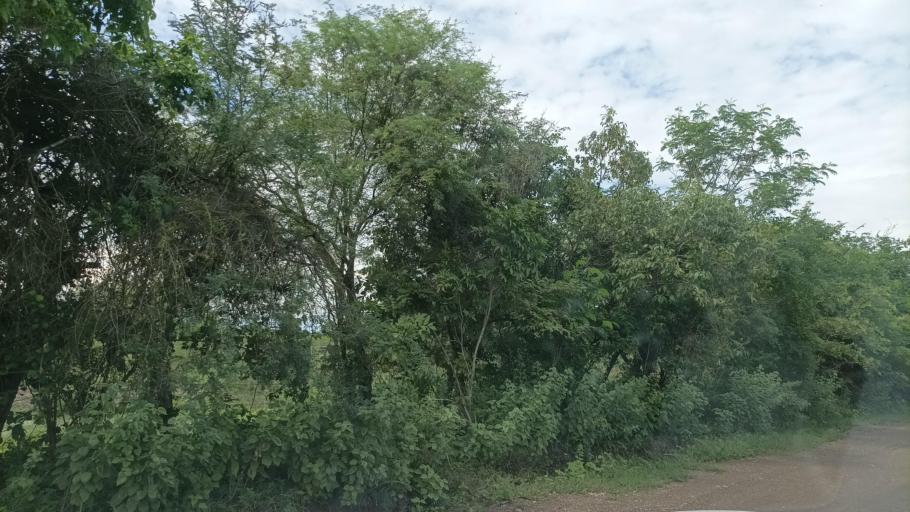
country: MX
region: Veracruz
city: Panuco
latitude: 21.9436
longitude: -98.1389
